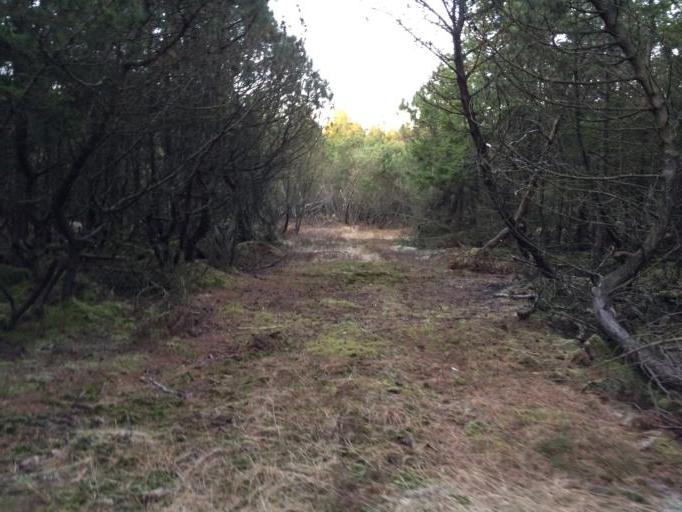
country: DK
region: Central Jutland
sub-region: Holstebro Kommune
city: Ulfborg
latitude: 56.2542
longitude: 8.4492
